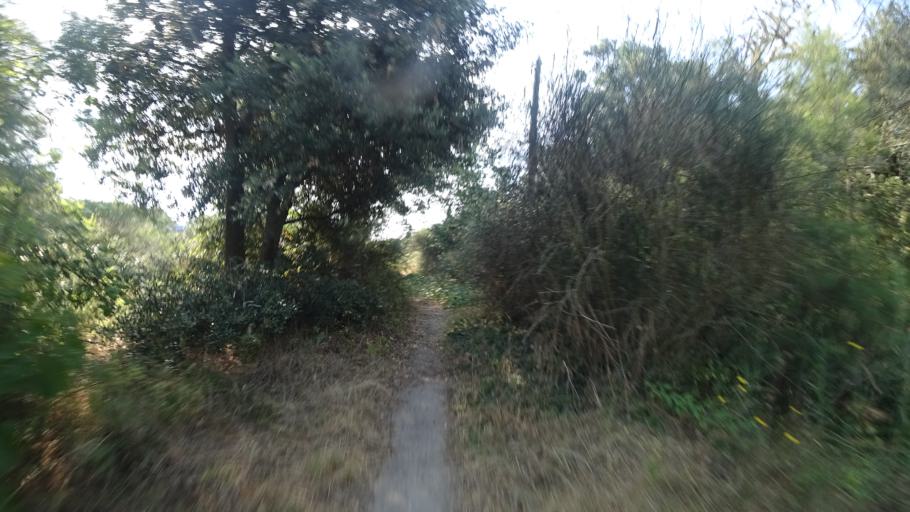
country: FR
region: Languedoc-Roussillon
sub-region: Departement des Pyrenees-Orientales
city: Canet-en-Roussillon
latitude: 42.6899
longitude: 3.0266
